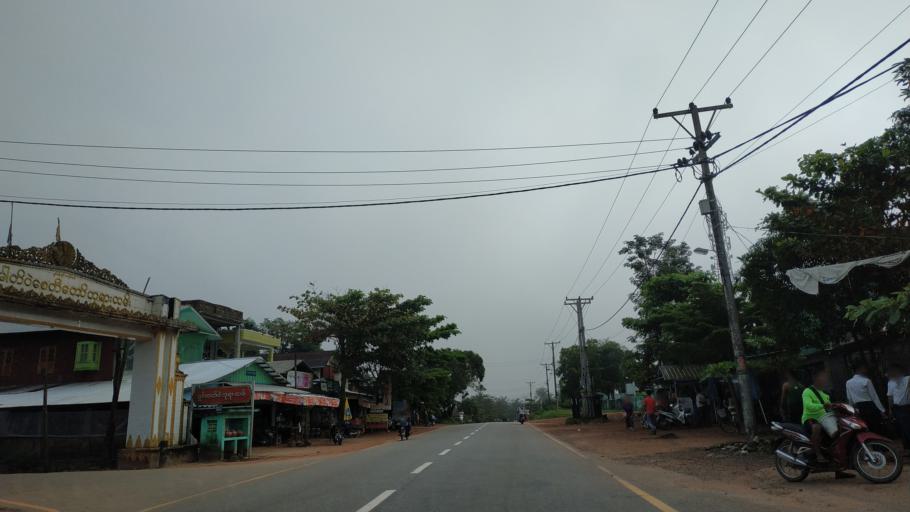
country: MM
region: Tanintharyi
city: Dawei
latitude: 14.1574
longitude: 98.2035
